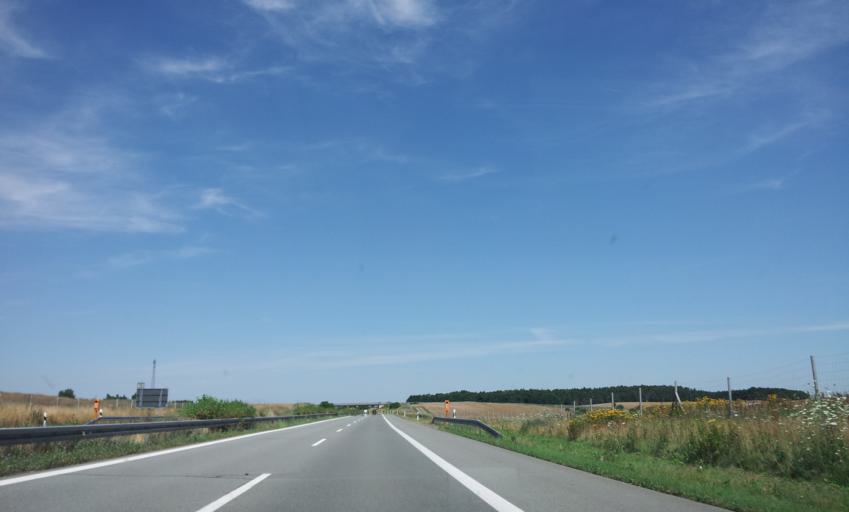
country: DE
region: Mecklenburg-Vorpommern
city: Neverin
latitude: 53.6321
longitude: 13.3678
